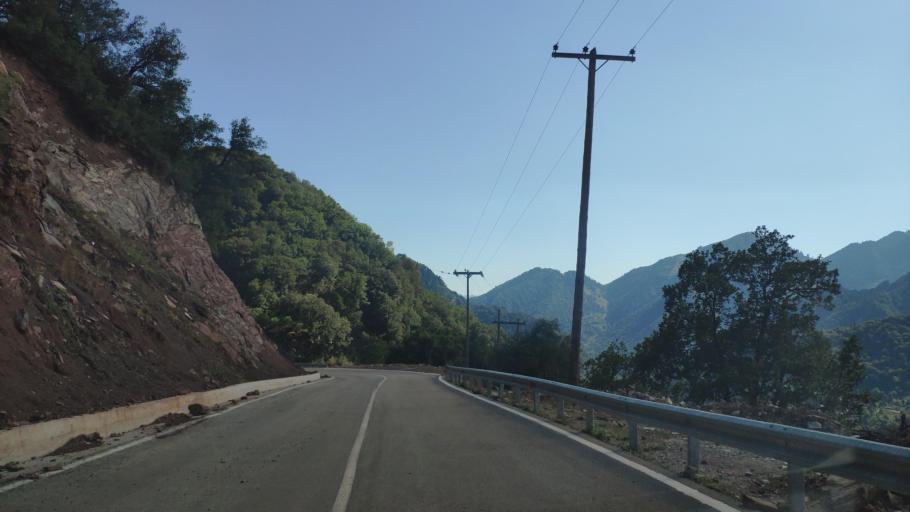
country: GR
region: Central Greece
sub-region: Nomos Evrytanias
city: Kerasochori
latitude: 39.1038
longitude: 21.6098
